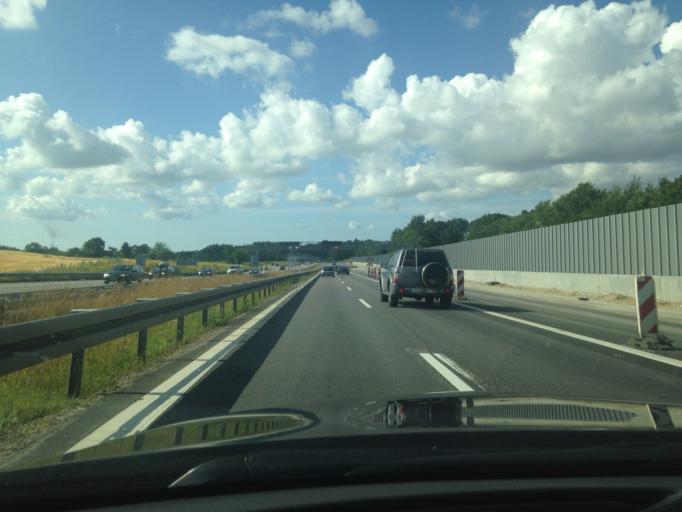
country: DK
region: Capital Region
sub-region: Horsholm Kommune
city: Horsholm
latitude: 55.8536
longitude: 12.4991
